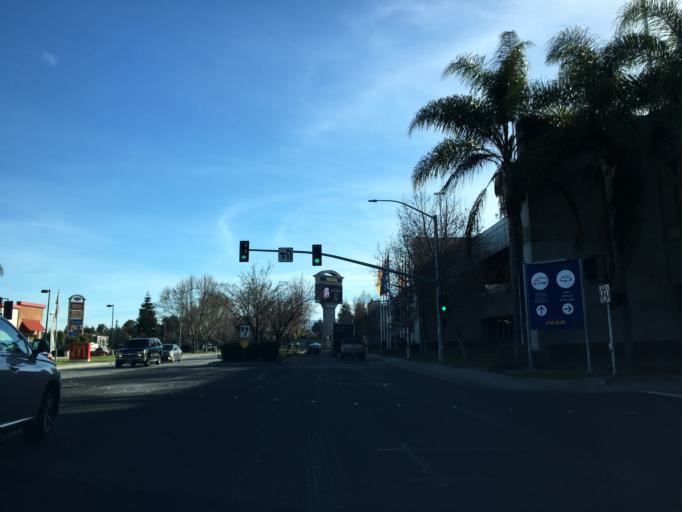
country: US
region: California
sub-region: San Mateo County
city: East Palo Alto
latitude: 37.4608
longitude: -122.1382
